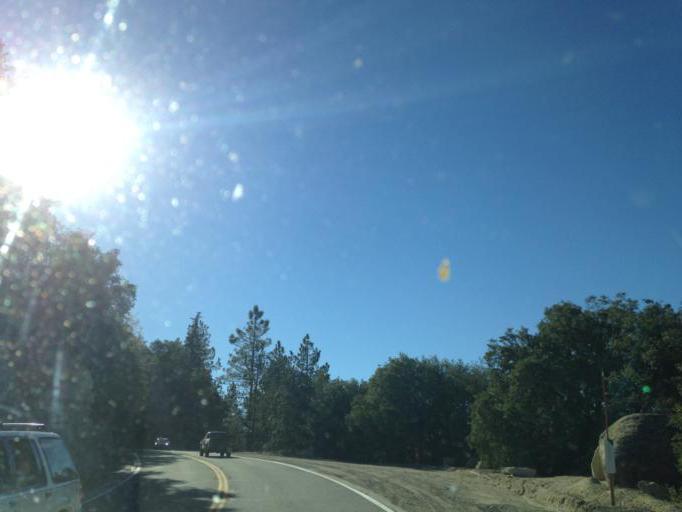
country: US
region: California
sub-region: Riverside County
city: Idyllwild-Pine Cove
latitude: 33.7915
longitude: -116.7481
